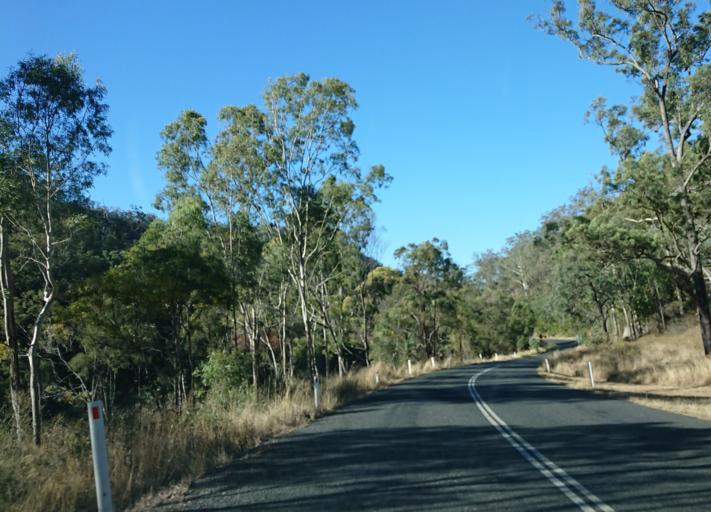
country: AU
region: Queensland
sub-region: Toowoomba
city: Top Camp
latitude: -27.7508
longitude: 152.0831
